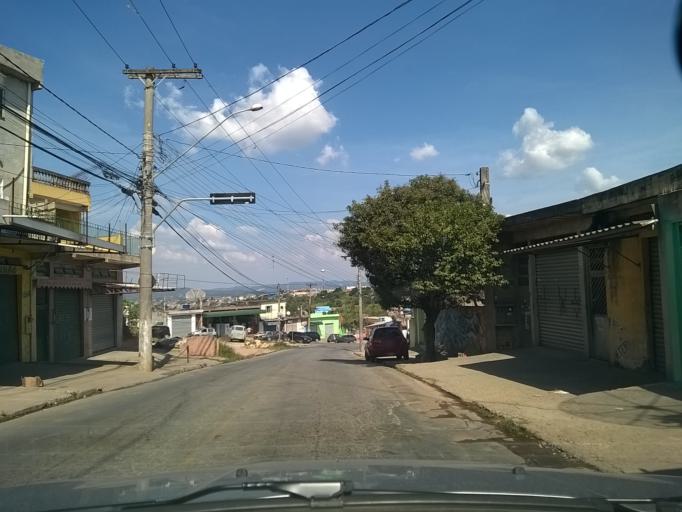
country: BR
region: Sao Paulo
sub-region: Francisco Morato
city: Francisco Morato
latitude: -23.2658
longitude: -46.7413
